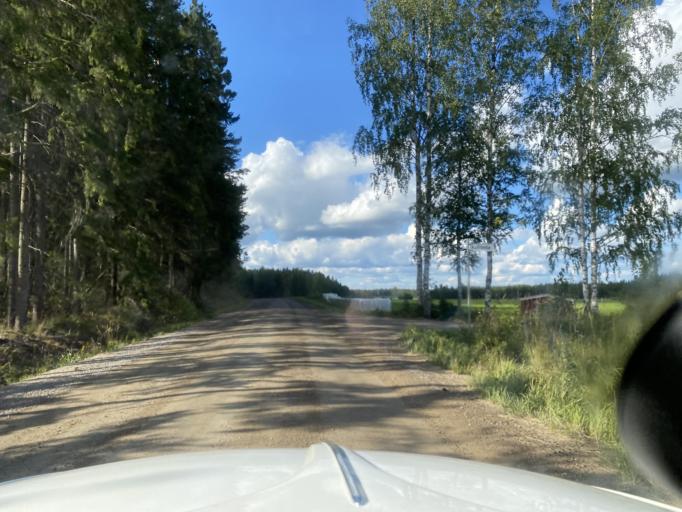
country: FI
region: Pirkanmaa
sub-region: Lounais-Pirkanmaa
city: Punkalaidun
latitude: 61.1159
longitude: 23.2731
